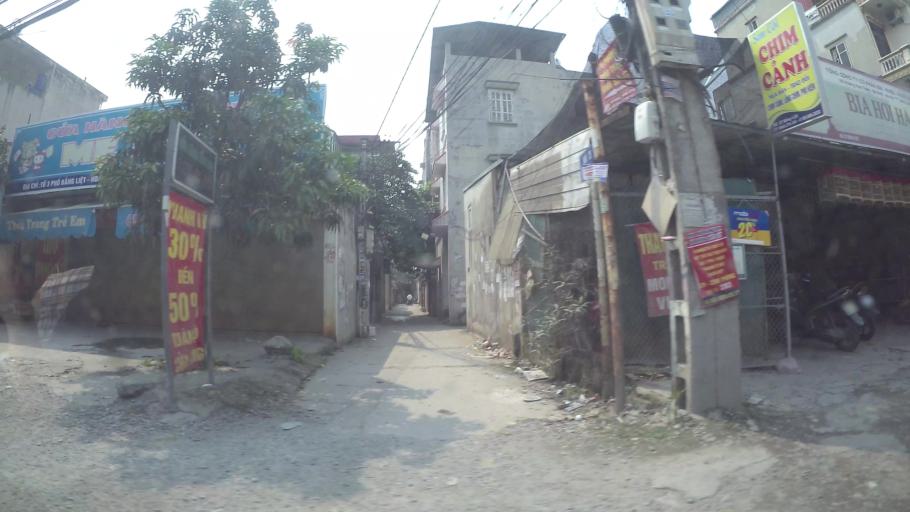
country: VN
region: Ha Noi
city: Van Dien
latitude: 20.9645
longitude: 105.8201
